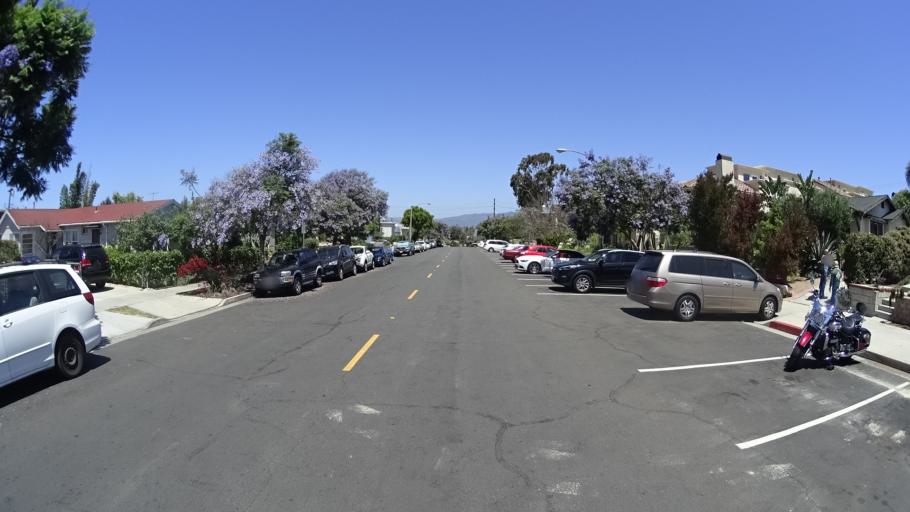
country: US
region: California
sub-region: Los Angeles County
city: Santa Monica
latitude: 34.0158
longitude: -118.4796
